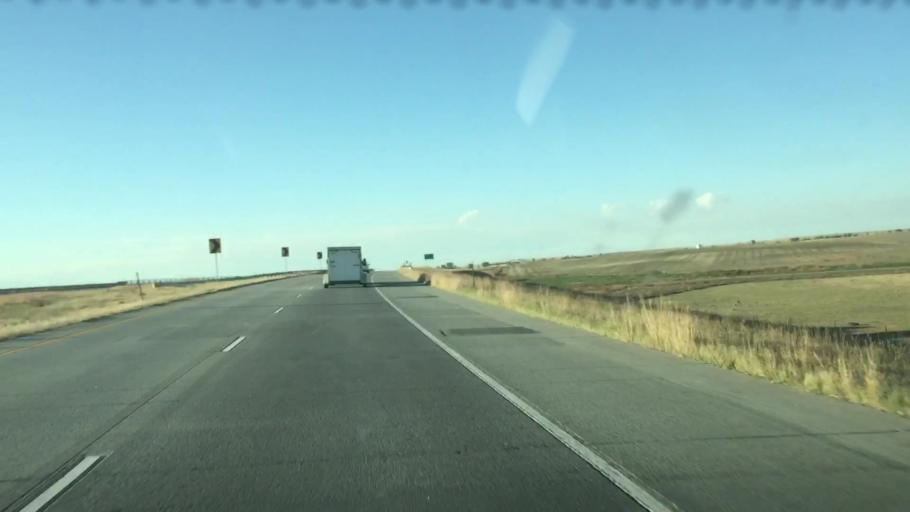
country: US
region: Colorado
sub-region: Arapahoe County
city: Byers
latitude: 39.5937
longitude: -104.0321
